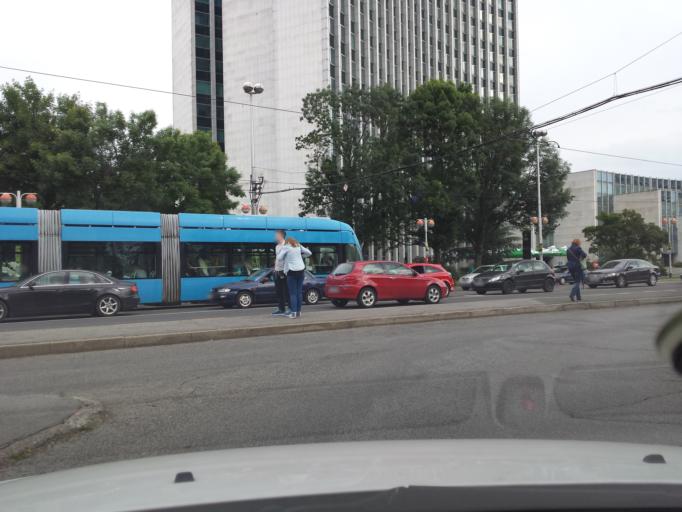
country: HR
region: Grad Zagreb
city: Zagreb - Centar
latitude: 45.7991
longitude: 15.9618
